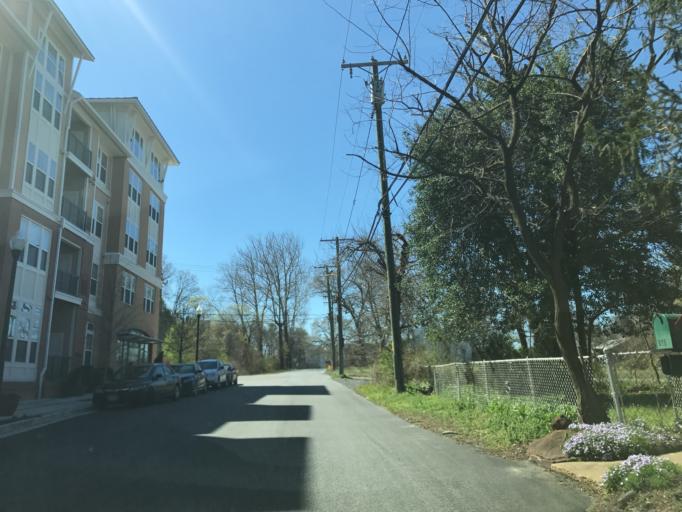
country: US
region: Maryland
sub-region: Anne Arundel County
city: Odenton
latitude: 39.0923
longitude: -76.7099
